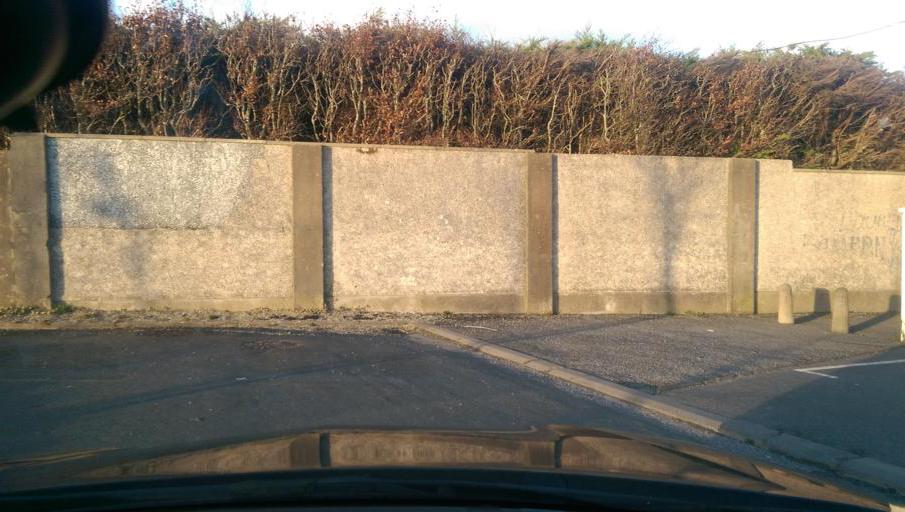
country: IE
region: Connaught
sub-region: County Galway
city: Gaillimh
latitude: 53.2900
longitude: -9.0819
